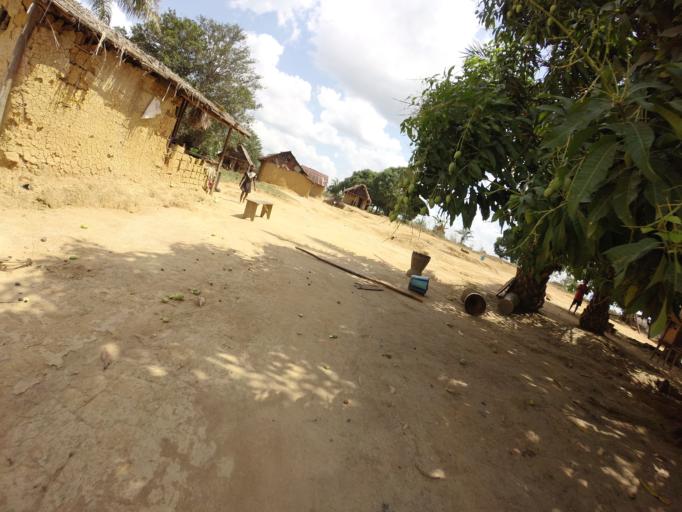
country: SL
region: Eastern Province
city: Jojoima
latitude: 7.7691
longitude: -10.5359
